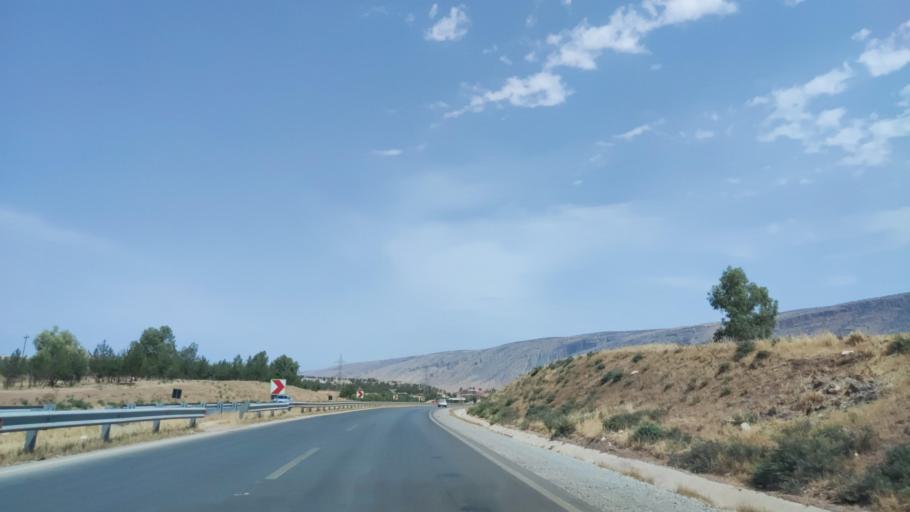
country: IQ
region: Arbil
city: Shaqlawah
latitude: 36.4765
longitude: 44.3807
